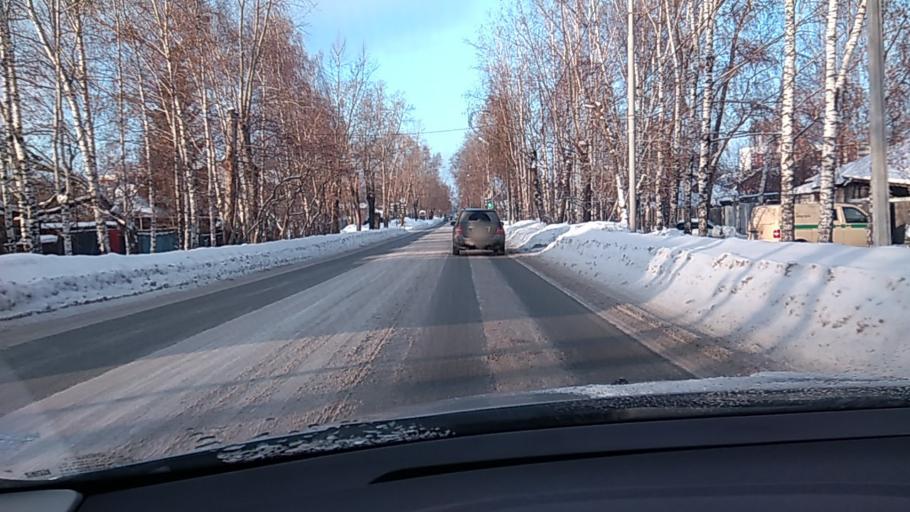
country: RU
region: Sverdlovsk
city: Yekaterinburg
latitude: 56.8081
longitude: 60.5875
